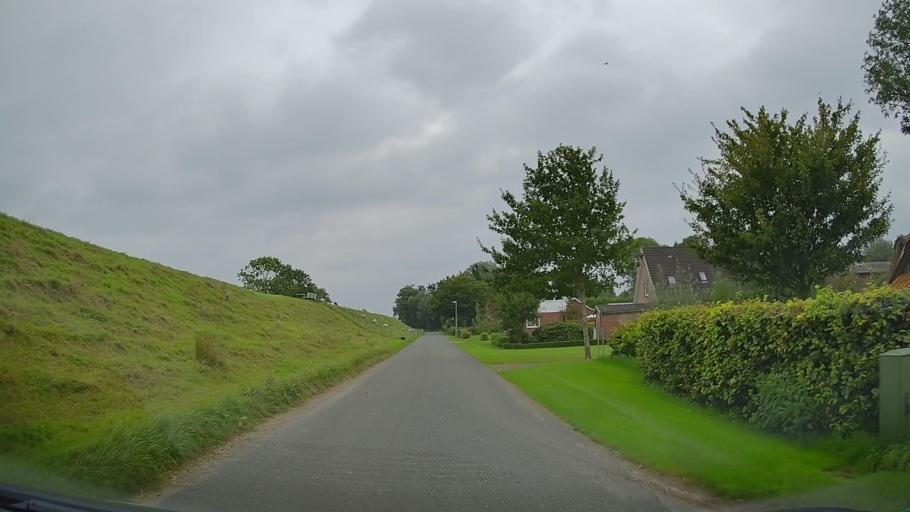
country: DE
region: Lower Saxony
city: Balje
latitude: 53.8306
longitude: 9.1457
